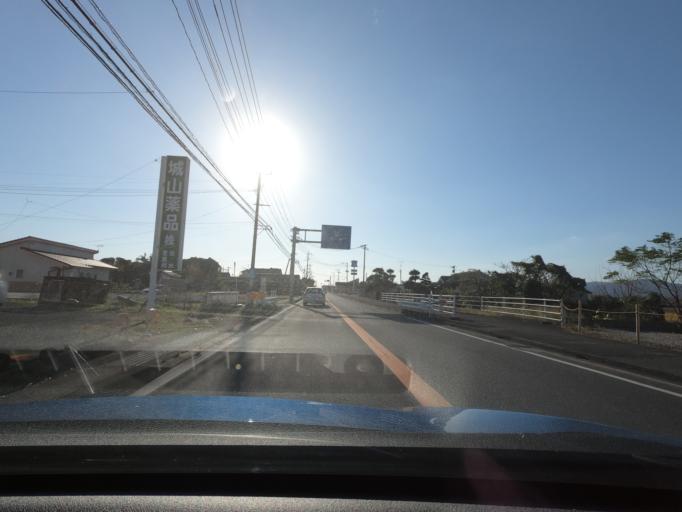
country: JP
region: Kagoshima
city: Izumi
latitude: 32.1031
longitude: 130.3135
